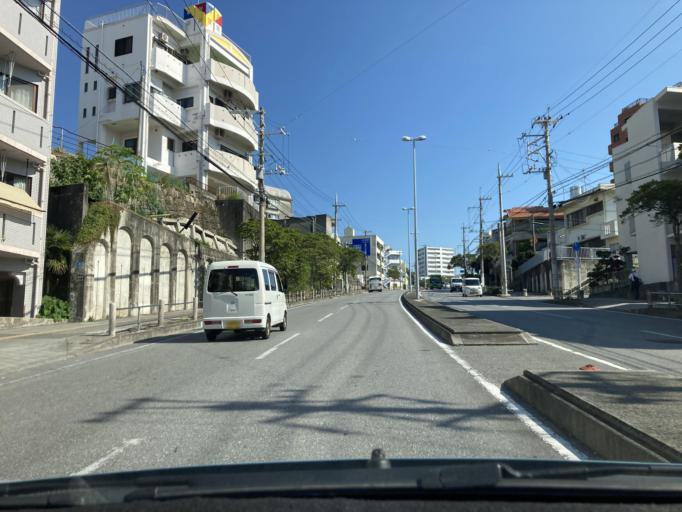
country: JP
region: Okinawa
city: Naha-shi
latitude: 26.2046
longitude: 127.7046
